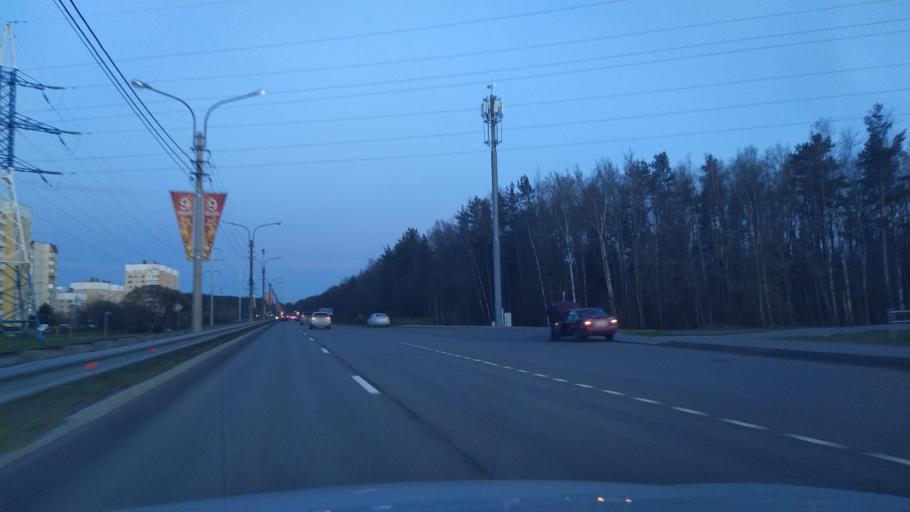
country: RU
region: St.-Petersburg
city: Razliv
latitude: 60.0801
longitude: 29.9604
